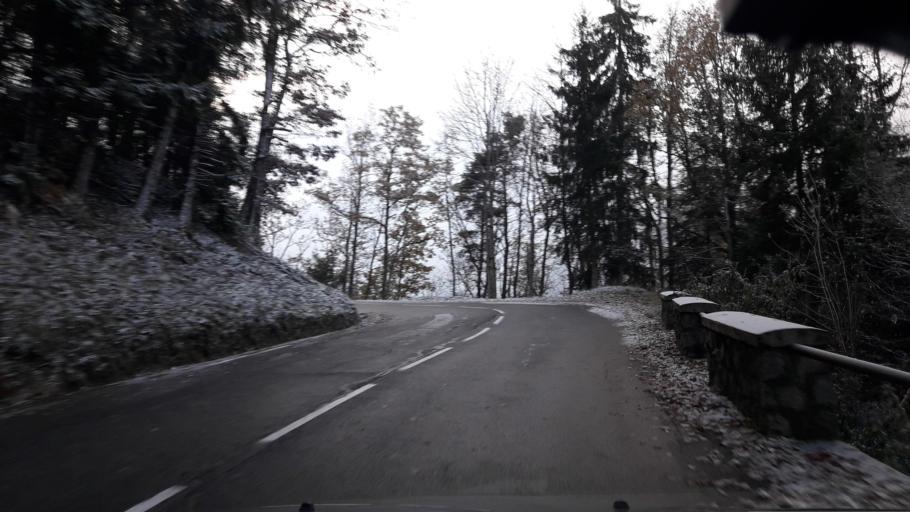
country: FR
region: Rhone-Alpes
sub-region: Departement de l'Isere
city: Allevard
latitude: 45.3847
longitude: 6.0926
